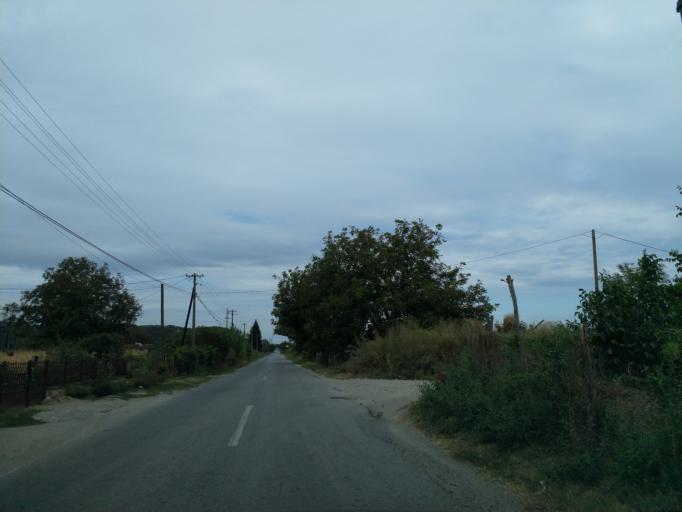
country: RS
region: Central Serbia
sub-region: Pomoravski Okrug
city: Cuprija
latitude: 43.9378
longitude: 21.3208
